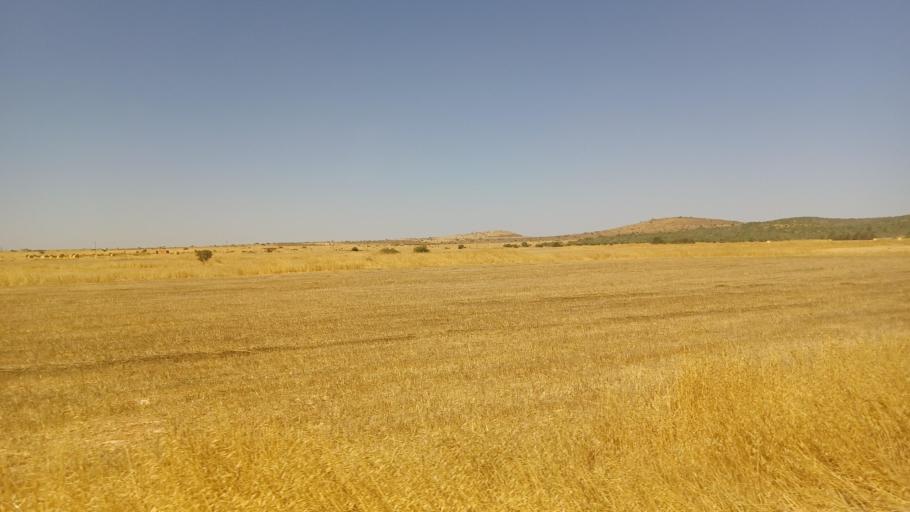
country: CY
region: Larnaka
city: Pergamos
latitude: 35.0424
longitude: 33.6827
